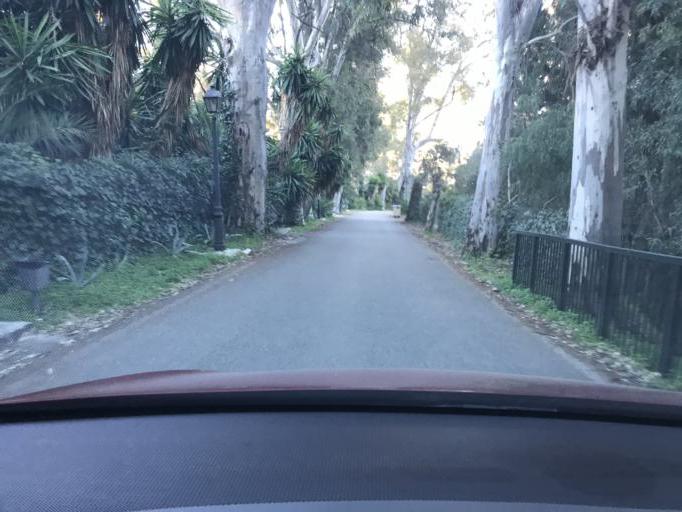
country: ES
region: Andalusia
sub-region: Provincia de Malaga
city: Tolox
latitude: 36.6809
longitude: -4.9084
